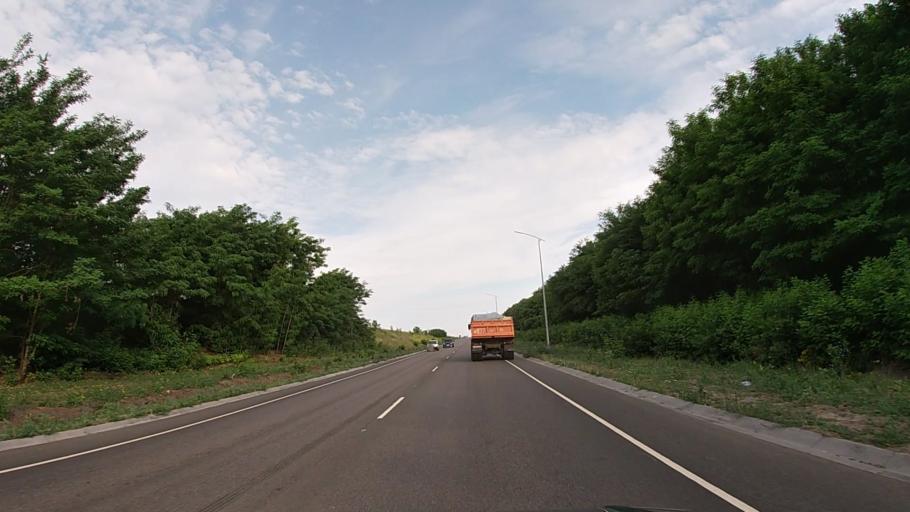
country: RU
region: Belgorod
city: Severnyy
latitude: 50.6691
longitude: 36.4884
